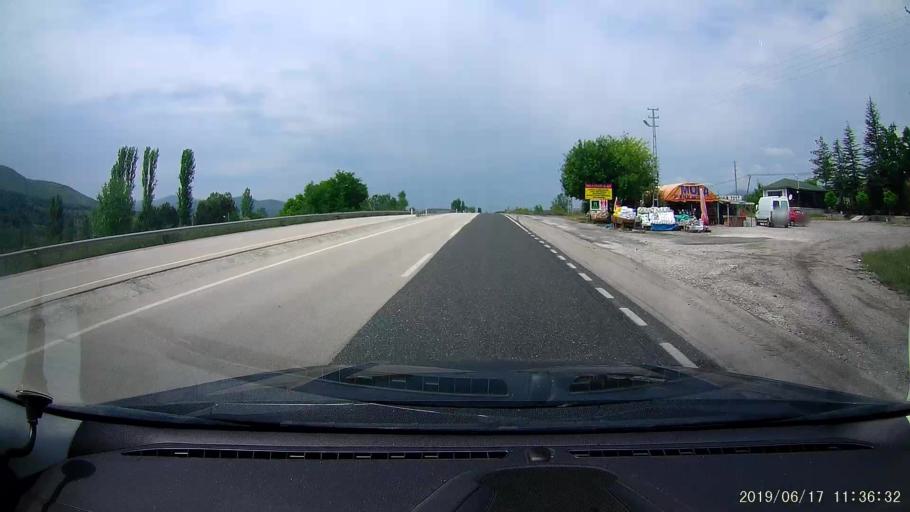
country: TR
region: Cankiri
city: Beloren
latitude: 40.8538
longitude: 33.4462
